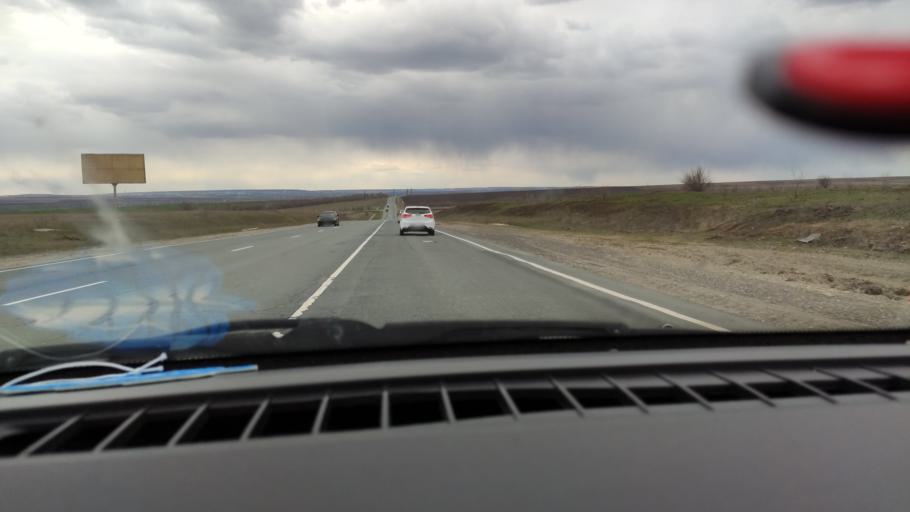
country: RU
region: Saratov
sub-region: Saratovskiy Rayon
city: Saratov
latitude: 51.7571
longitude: 46.0673
